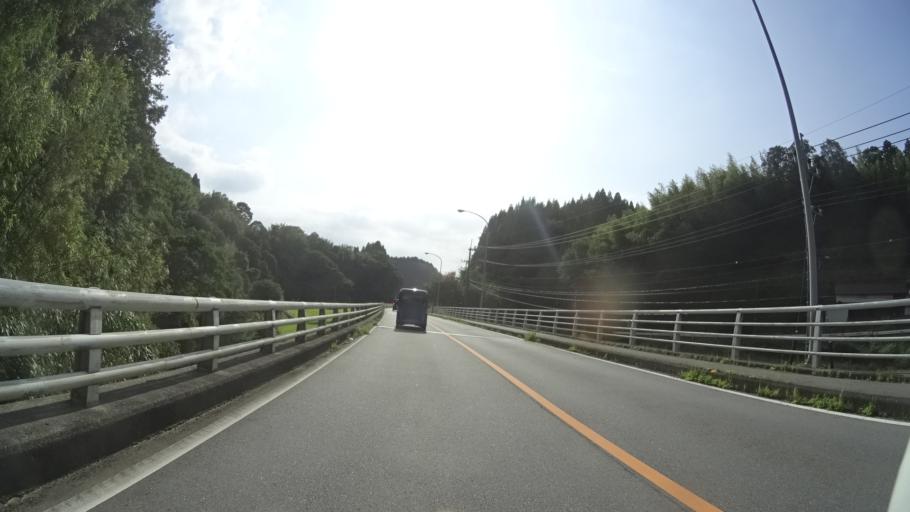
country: JP
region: Kumamoto
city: Aso
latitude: 32.6879
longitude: 131.0691
